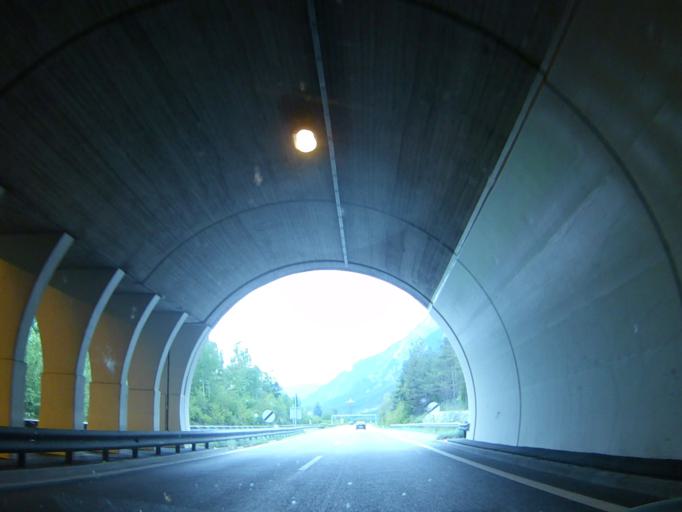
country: AT
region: Tyrol
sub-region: Politischer Bezirk Imst
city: Silz
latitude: 47.2695
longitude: 10.9068
